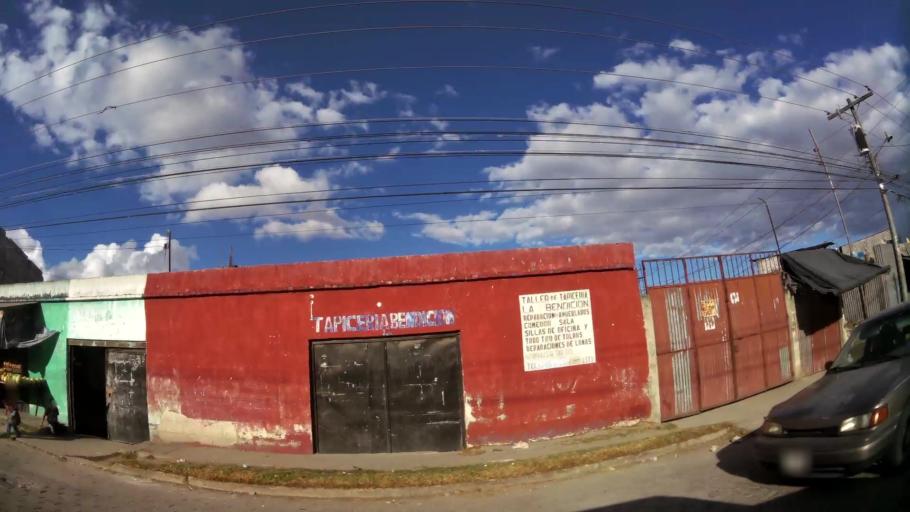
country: GT
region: Quetzaltenango
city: Quetzaltenango
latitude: 14.8528
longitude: -91.5248
